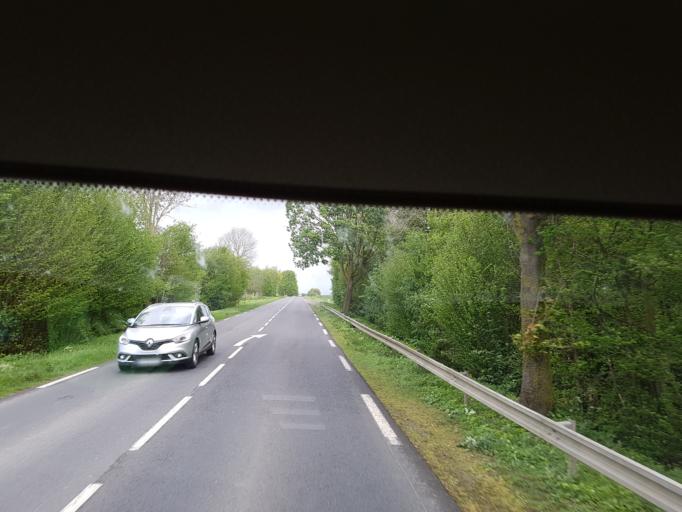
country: FR
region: Picardie
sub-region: Departement de l'Aisne
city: Saint-Quentin
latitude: 49.8842
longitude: 3.2668
